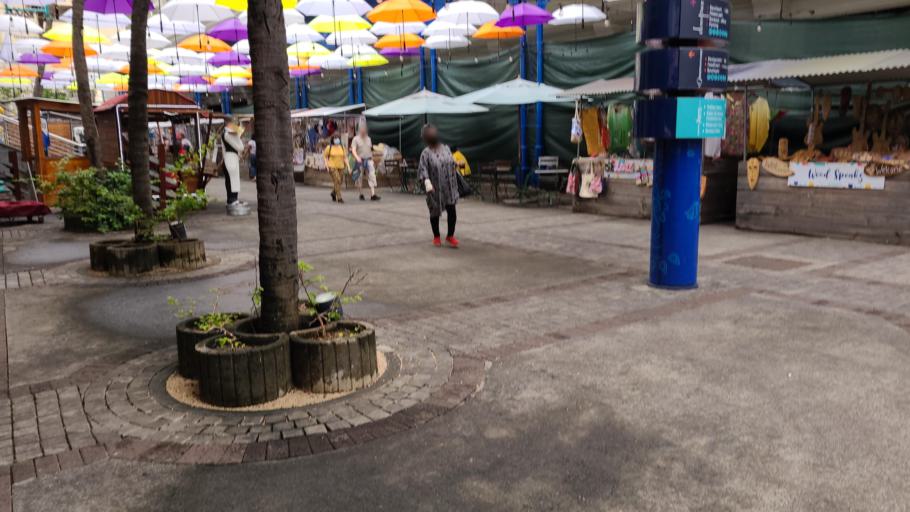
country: MU
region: Port Louis
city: Port Louis
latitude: -20.1610
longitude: 57.4982
